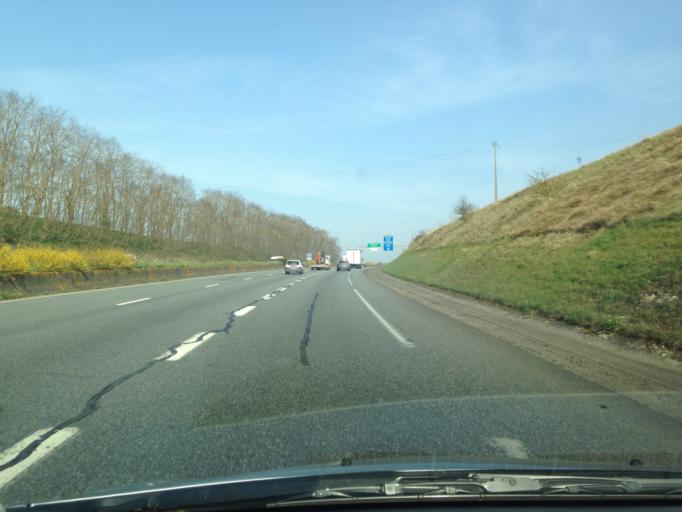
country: FR
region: Picardie
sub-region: Departement de la Somme
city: Abbeville
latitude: 50.1310
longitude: 1.8068
